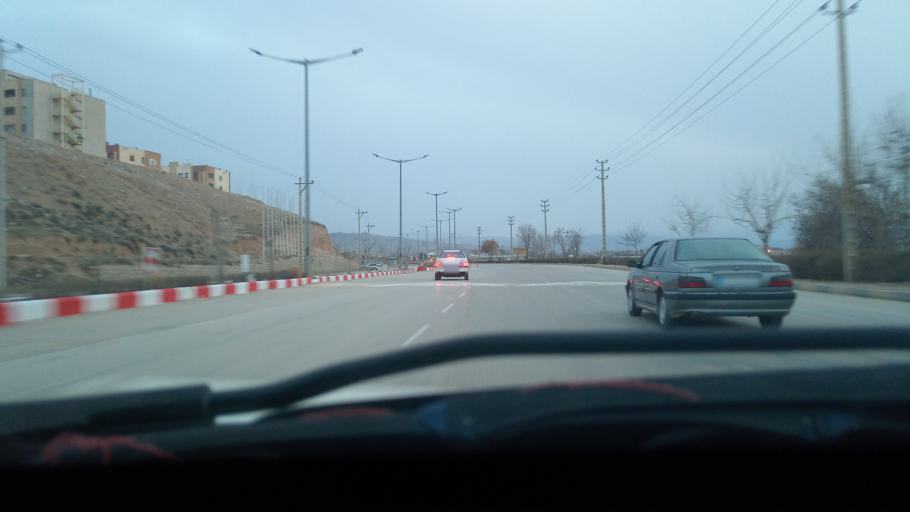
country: IR
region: Khorasan-e Shomali
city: Bojnurd
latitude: 37.4496
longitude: 57.3166
